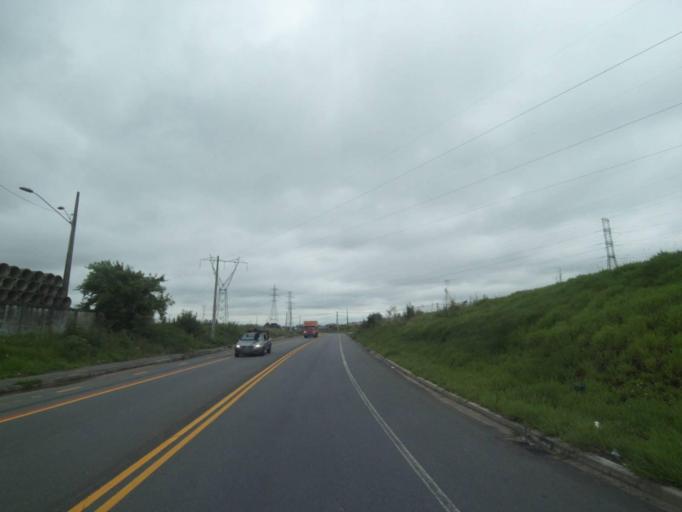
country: BR
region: Parana
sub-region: Araucaria
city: Araucaria
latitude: -25.5231
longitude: -49.3352
